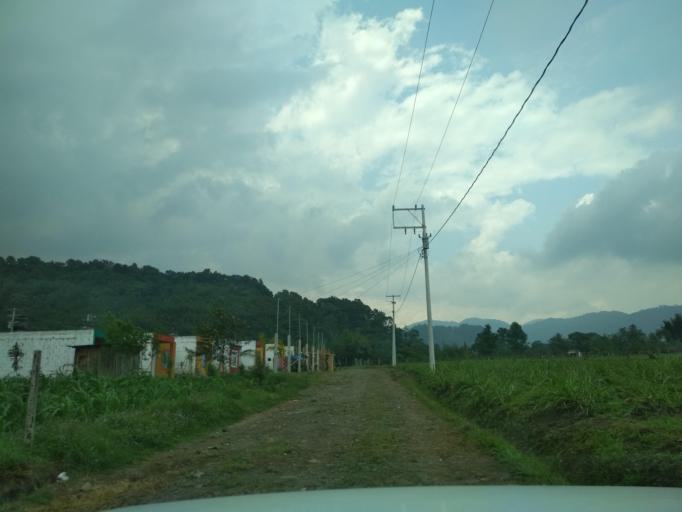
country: MX
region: Veracruz
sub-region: Mariano Escobedo
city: Mariano Escobedo
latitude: 18.9156
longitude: -97.1362
